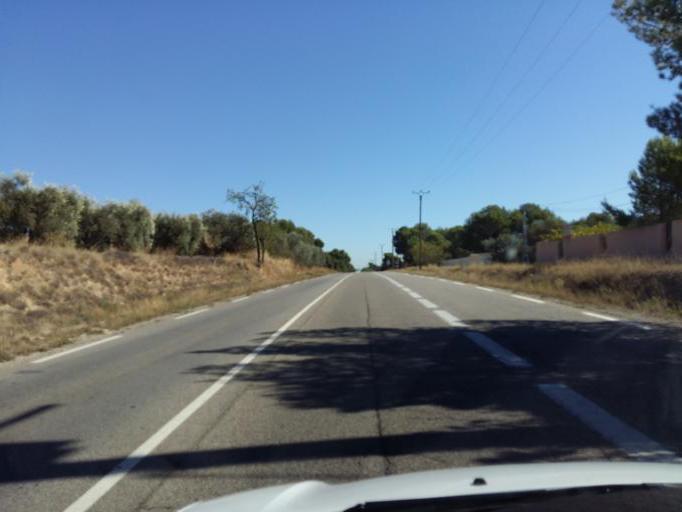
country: FR
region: Provence-Alpes-Cote d'Azur
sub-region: Departement du Vaucluse
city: Merindol
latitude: 43.7536
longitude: 5.1890
